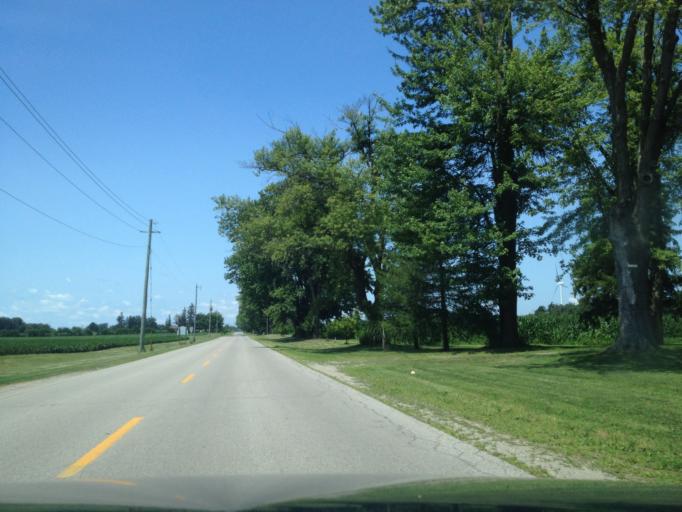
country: CA
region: Ontario
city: Aylmer
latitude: 42.6017
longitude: -80.6633
